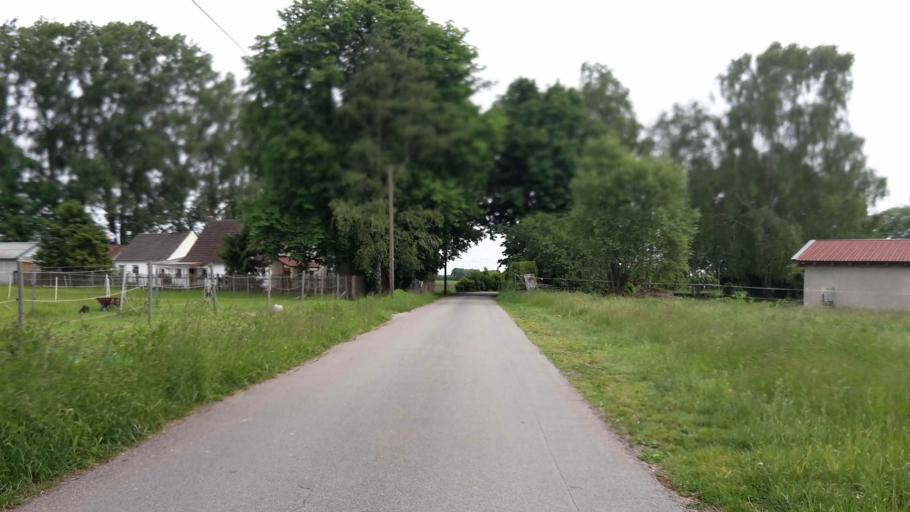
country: DE
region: Bavaria
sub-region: Upper Bavaria
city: Karlsfeld
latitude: 48.2208
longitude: 11.4356
